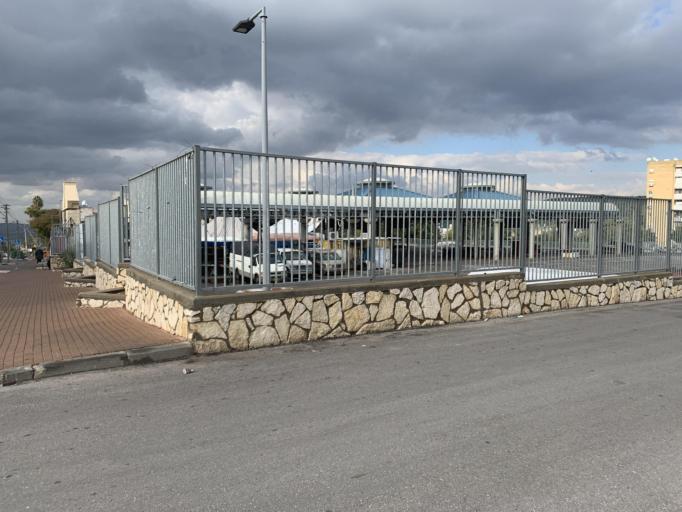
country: IL
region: Northern District
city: Migdal Ha`Emeq
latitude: 32.6794
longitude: 35.2379
